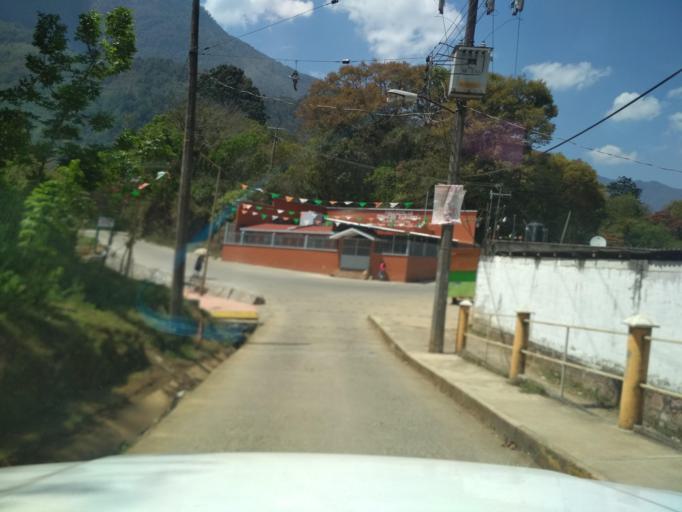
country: MX
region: Veracruz
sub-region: Tlilapan
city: Tonalixco
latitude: 18.7769
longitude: -97.0775
